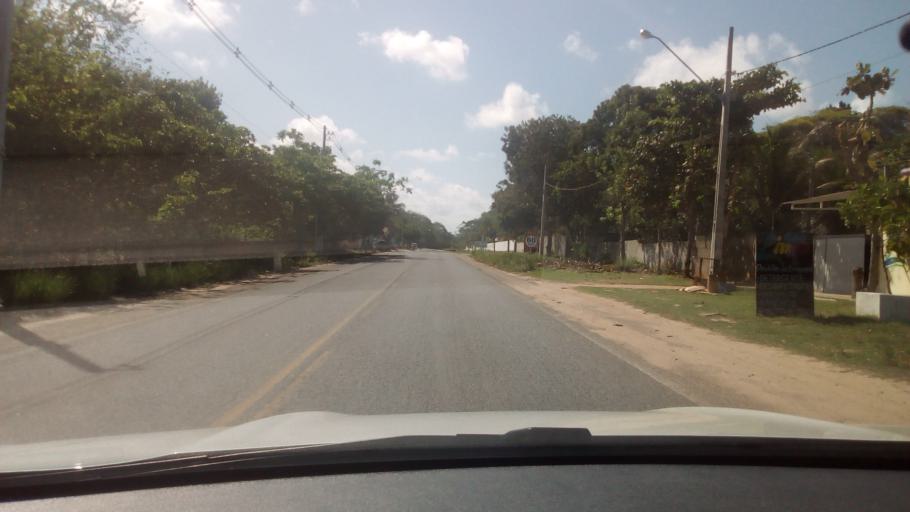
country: BR
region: Paraiba
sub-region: Joao Pessoa
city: Joao Pessoa
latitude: -7.1972
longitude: -34.8184
